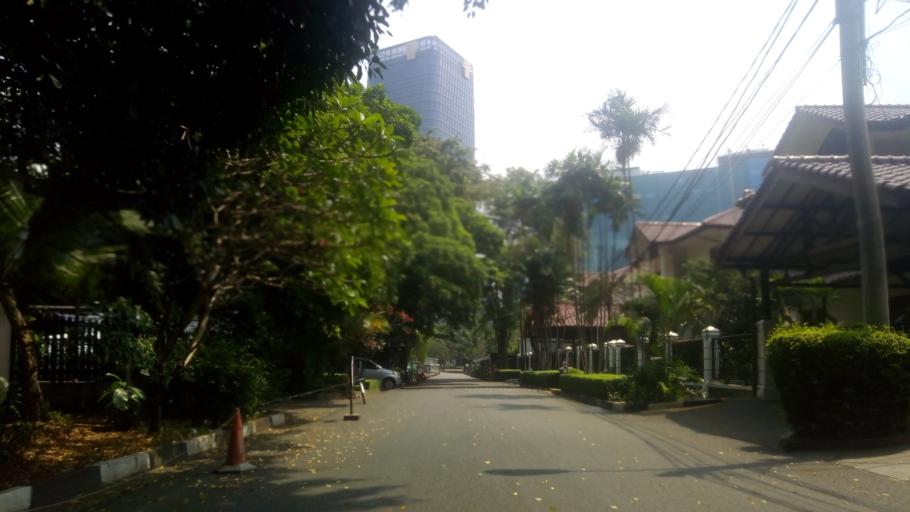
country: ID
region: Jakarta Raya
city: Jakarta
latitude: -6.2369
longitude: 106.8318
